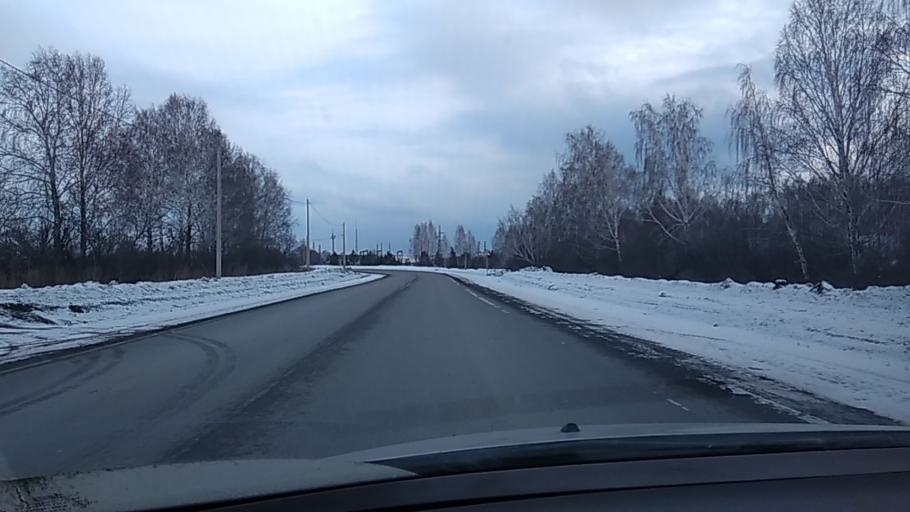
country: RU
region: Sverdlovsk
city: Sovkhoznyy
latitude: 56.6132
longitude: 61.2977
